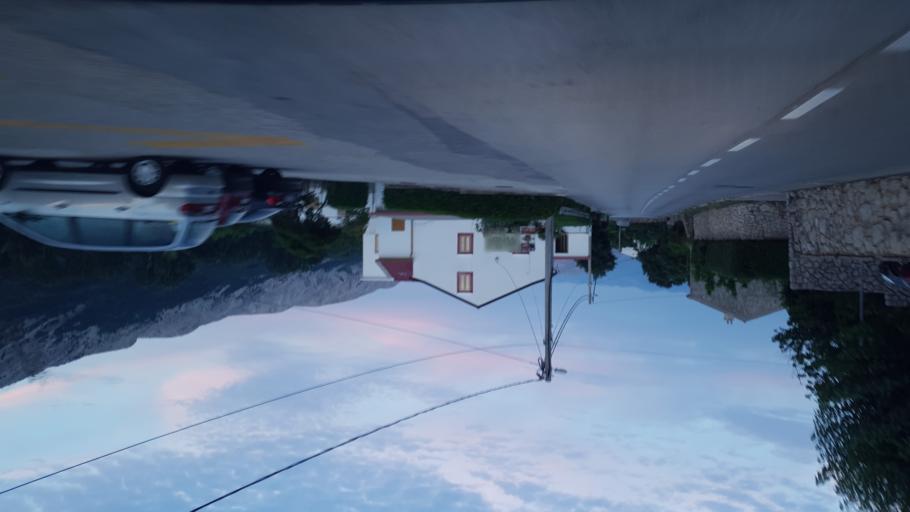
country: HR
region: Primorsko-Goranska
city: Punat
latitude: 44.9784
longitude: 14.7340
